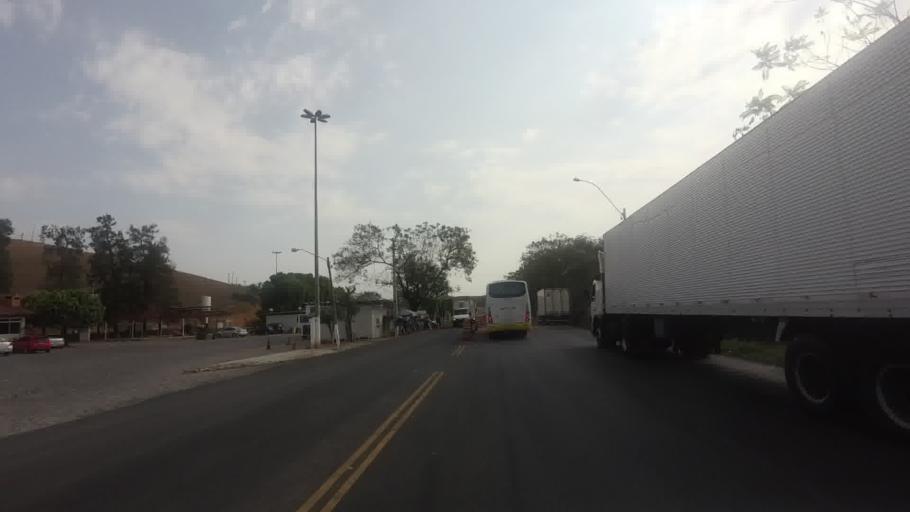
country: BR
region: Rio de Janeiro
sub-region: Itaperuna
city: Itaperuna
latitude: -21.2573
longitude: -41.7682
